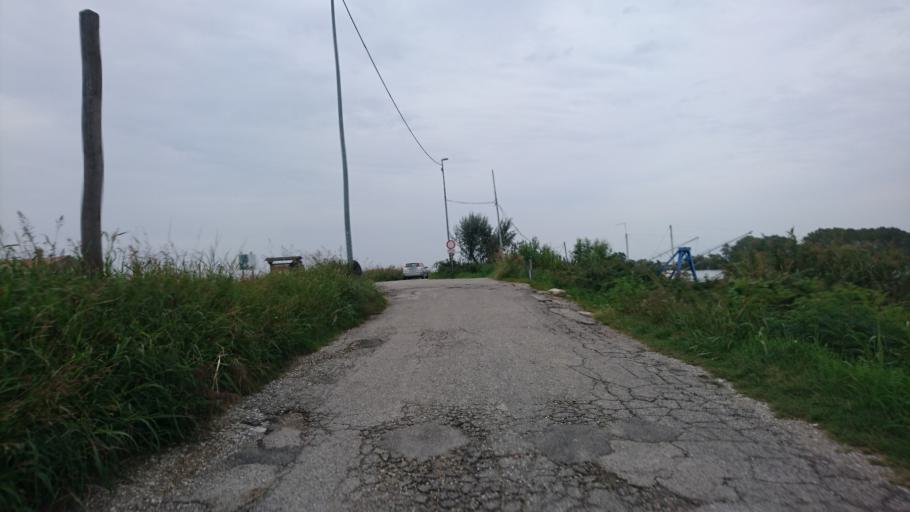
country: IT
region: Emilia-Romagna
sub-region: Provincia di Ferrara
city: Goro
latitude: 44.8395
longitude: 12.3735
